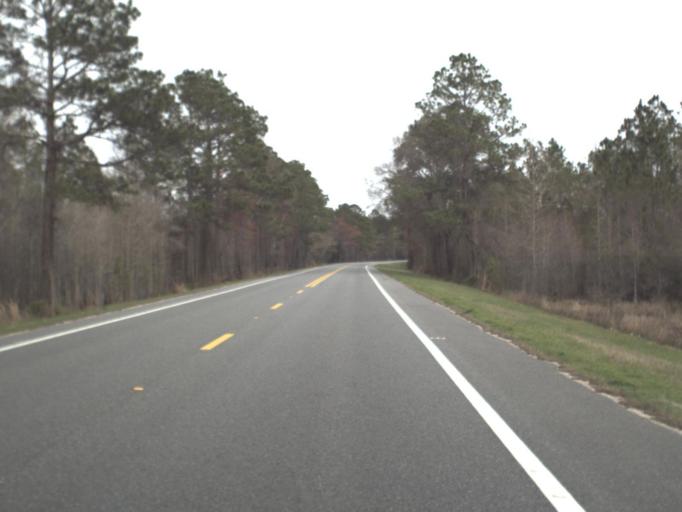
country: US
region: Florida
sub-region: Leon County
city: Woodville
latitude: 30.1877
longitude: -84.0272
